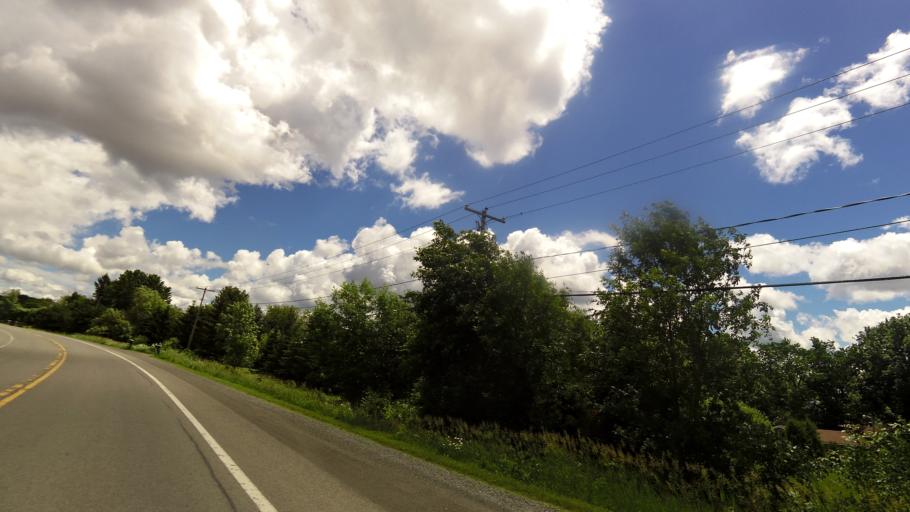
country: CA
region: Quebec
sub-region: Monteregie
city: Rigaud
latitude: 45.5263
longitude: -74.2214
